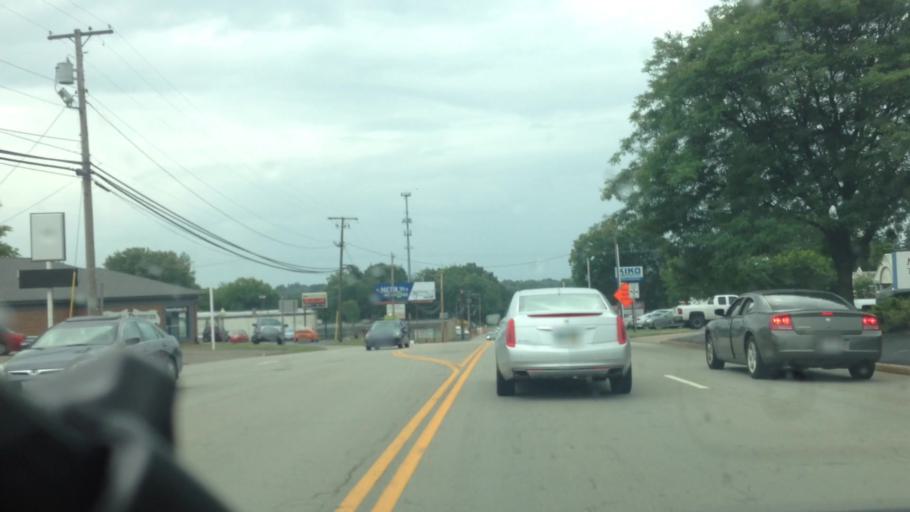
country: US
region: Ohio
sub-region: Stark County
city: Canton
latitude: 40.8269
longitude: -81.4030
